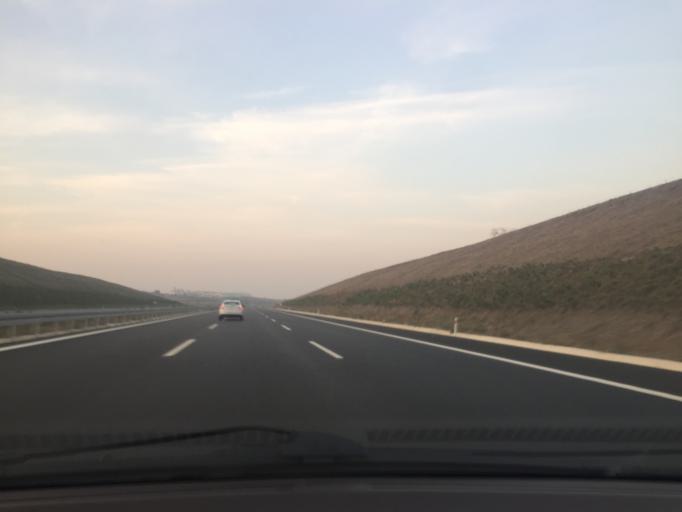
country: TR
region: Bursa
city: Karacabey
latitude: 40.2622
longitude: 28.4853
